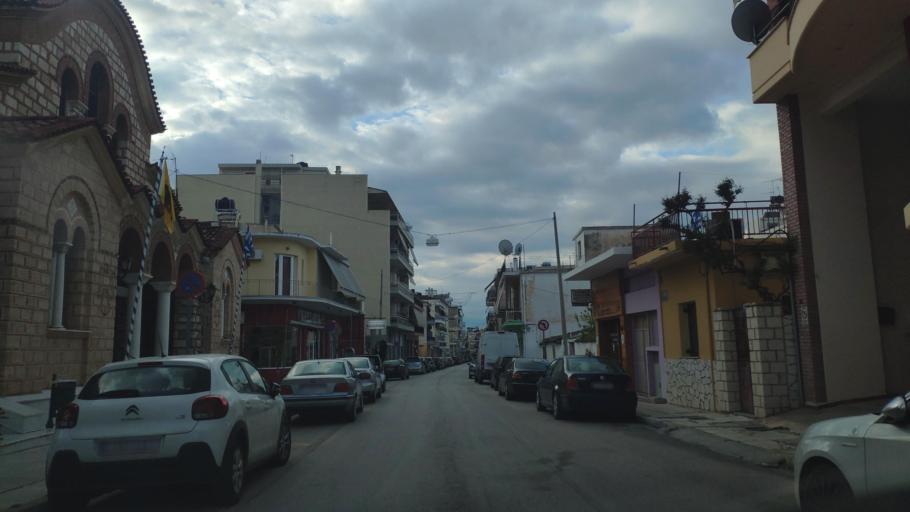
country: GR
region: Peloponnese
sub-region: Nomos Argolidos
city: Argos
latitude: 37.6414
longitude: 22.7293
